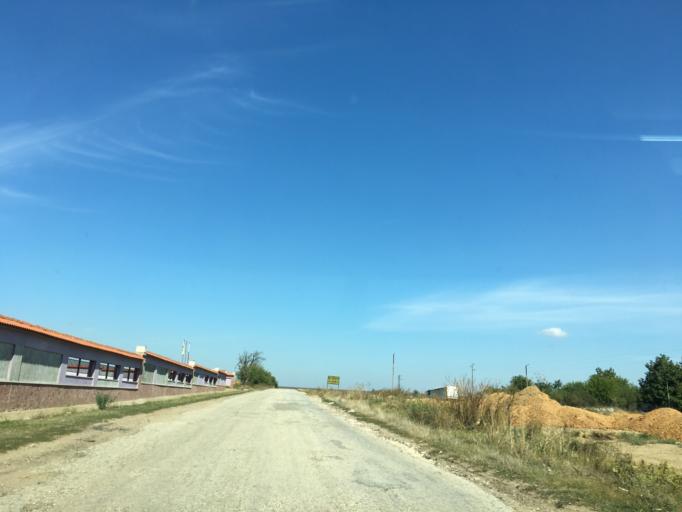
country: BG
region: Pleven
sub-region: Obshtina Knezha
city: Knezha
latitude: 43.5227
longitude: 24.0996
